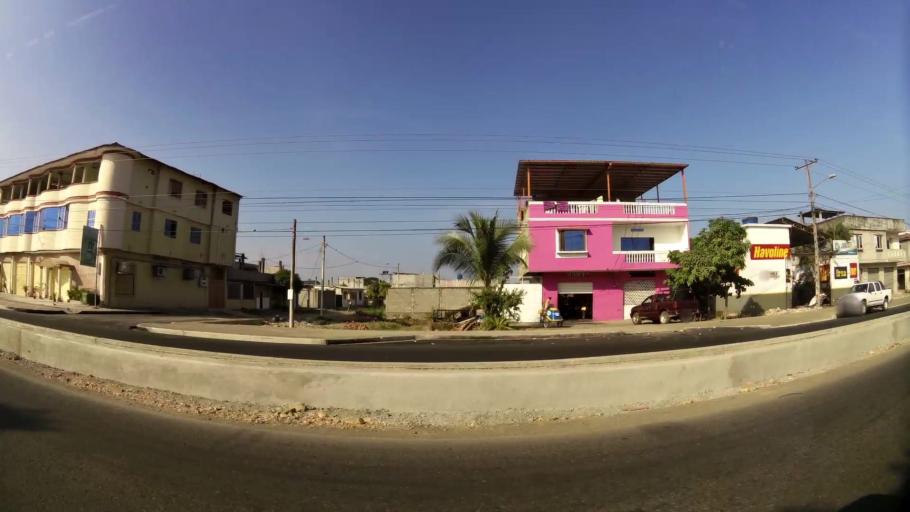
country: EC
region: Guayas
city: Eloy Alfaro
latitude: -2.1800
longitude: -79.8464
